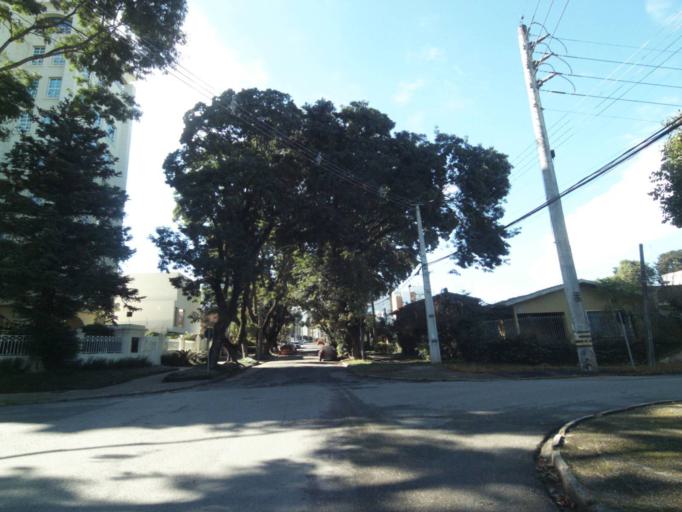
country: BR
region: Parana
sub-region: Curitiba
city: Curitiba
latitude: -25.4112
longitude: -49.2462
